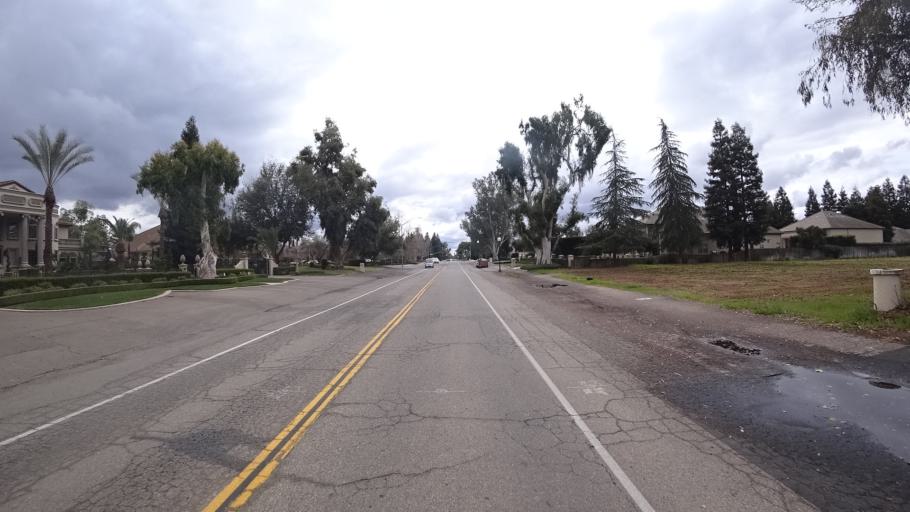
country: US
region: California
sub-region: Fresno County
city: Fresno
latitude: 36.8394
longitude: -119.8356
